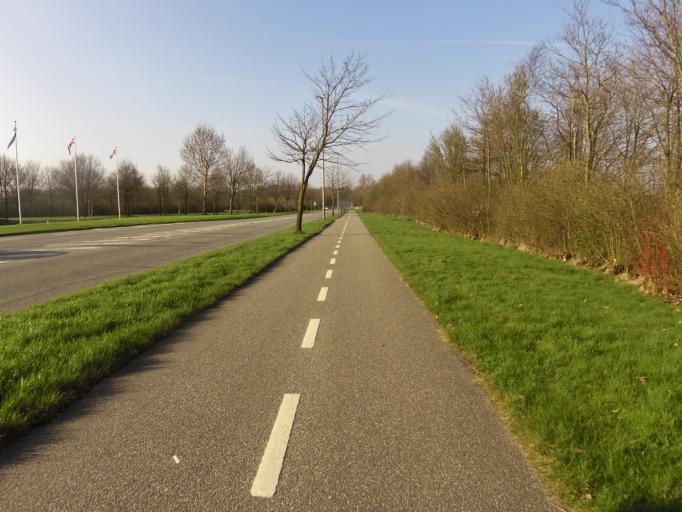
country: DK
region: South Denmark
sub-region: Vejen Kommune
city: Vejen
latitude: 55.4747
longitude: 9.1234
